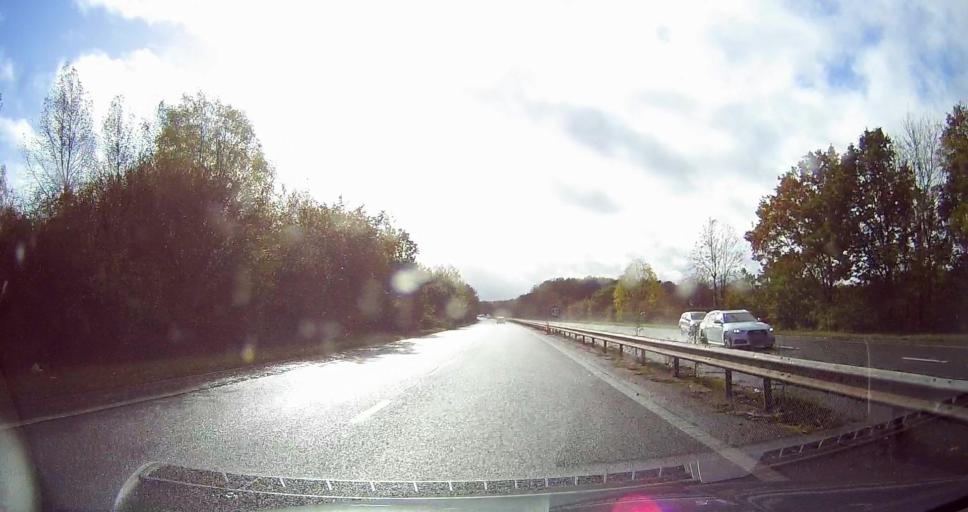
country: GB
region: England
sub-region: Warwickshire
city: Curdworth
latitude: 52.5458
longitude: -1.7776
